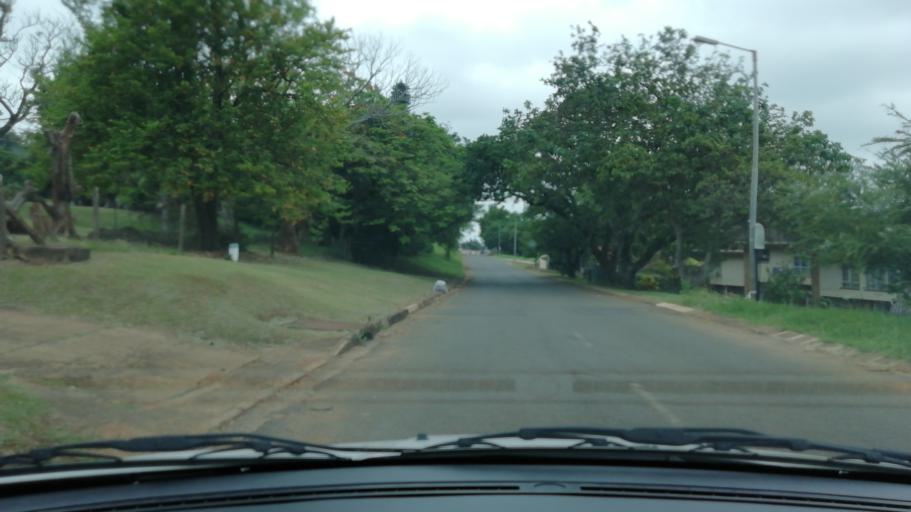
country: ZA
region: KwaZulu-Natal
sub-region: uThungulu District Municipality
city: Empangeni
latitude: -28.7461
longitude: 31.8932
